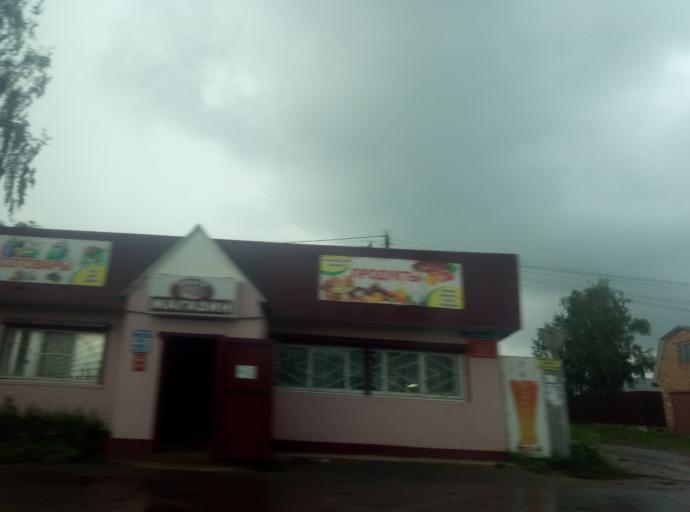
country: RU
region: Tula
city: Kireyevsk
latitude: 53.9907
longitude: 37.9282
